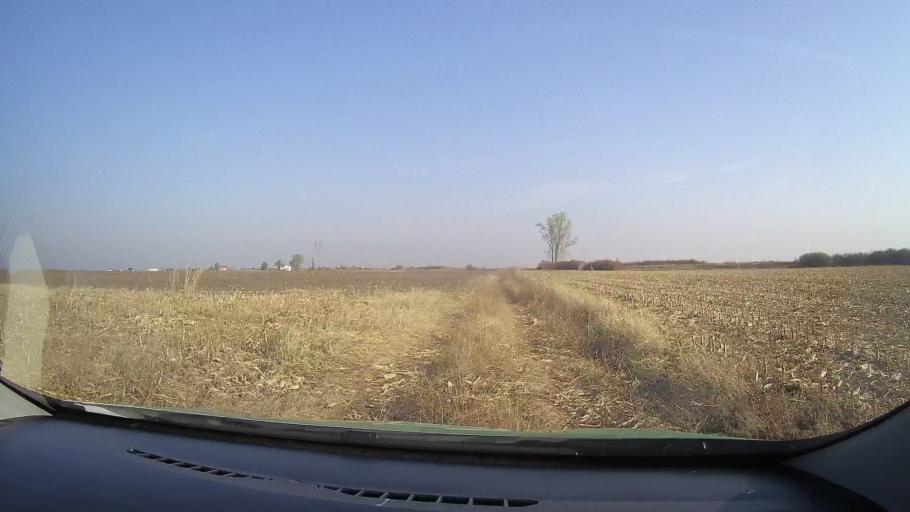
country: RO
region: Arad
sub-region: Comuna Pilu
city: Pilu
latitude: 46.5601
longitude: 21.3457
